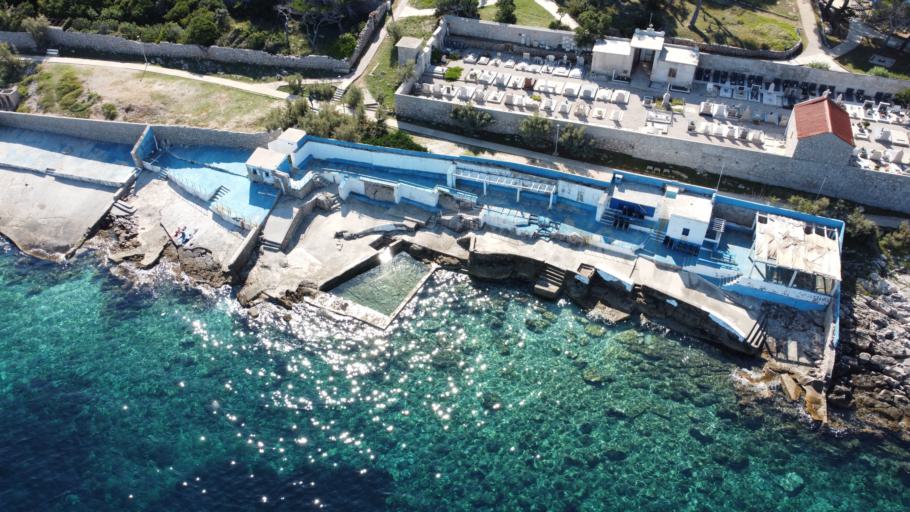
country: HR
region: Primorsko-Goranska
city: Mali Losinj
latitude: 44.5241
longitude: 14.5027
